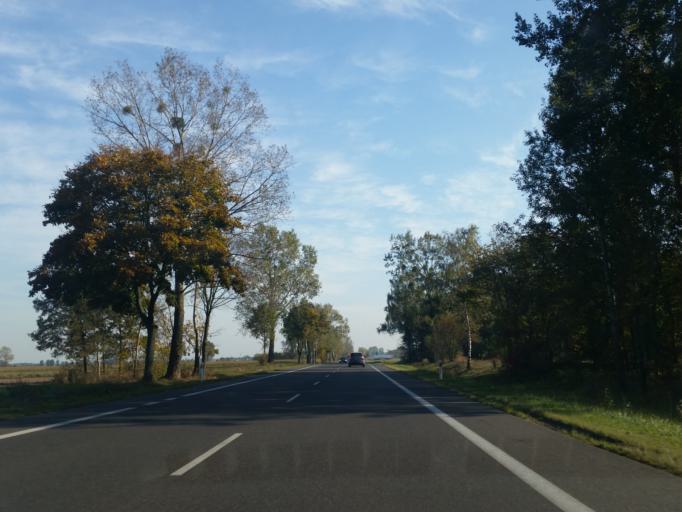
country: PL
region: Masovian Voivodeship
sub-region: Powiat plocki
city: Drobin
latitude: 52.7080
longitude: 20.0310
